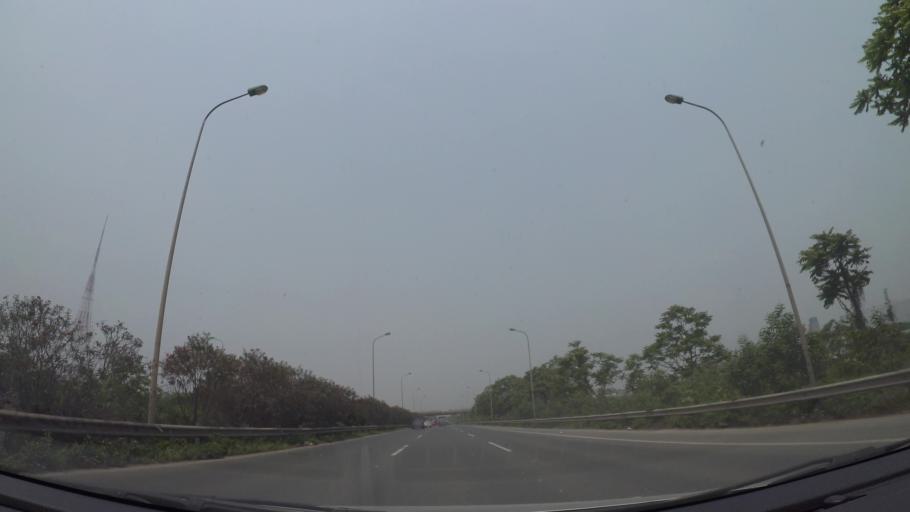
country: VN
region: Ha Noi
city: Thanh Xuan
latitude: 21.0054
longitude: 105.7683
